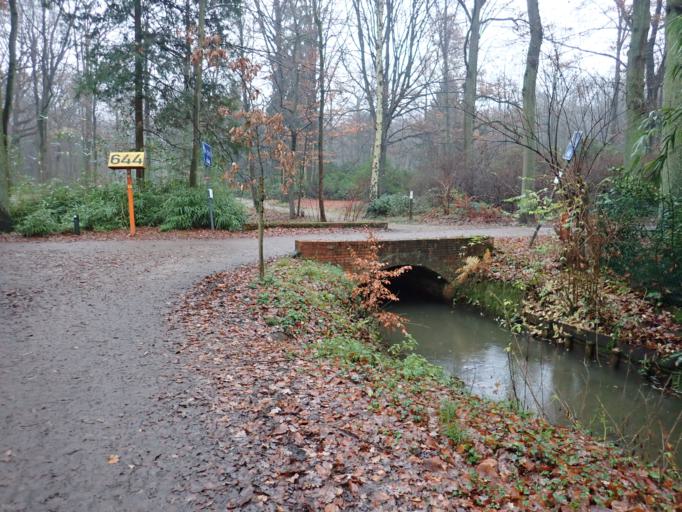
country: BE
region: Flanders
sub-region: Provincie Antwerpen
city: Brasschaat
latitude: 51.2808
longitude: 4.4930
